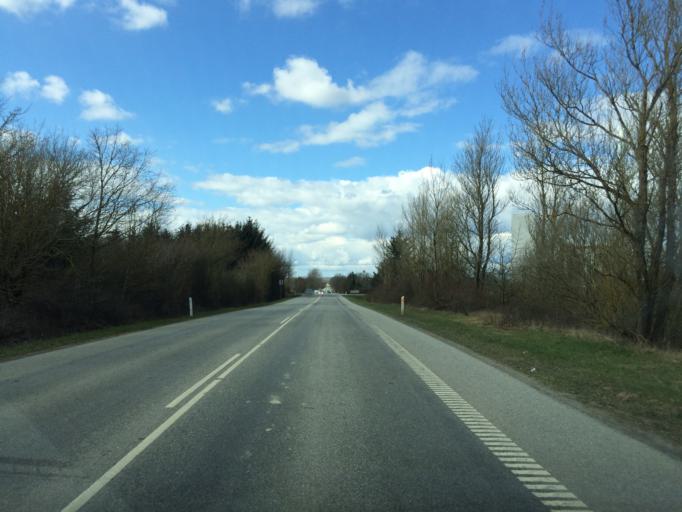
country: DK
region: South Denmark
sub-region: Assens Kommune
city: Arup
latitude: 55.4293
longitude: 10.0158
